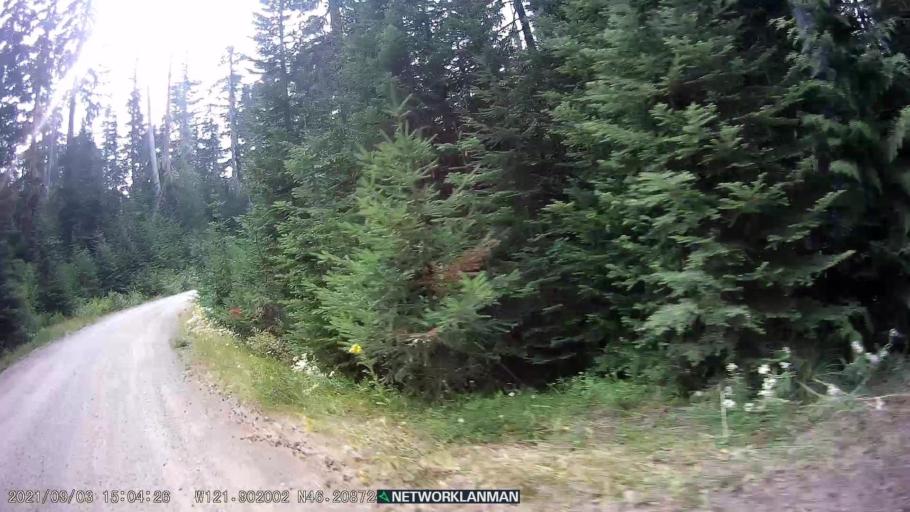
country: US
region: Washington
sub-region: Skamania County
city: Carson
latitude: 46.2089
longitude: -121.8995
